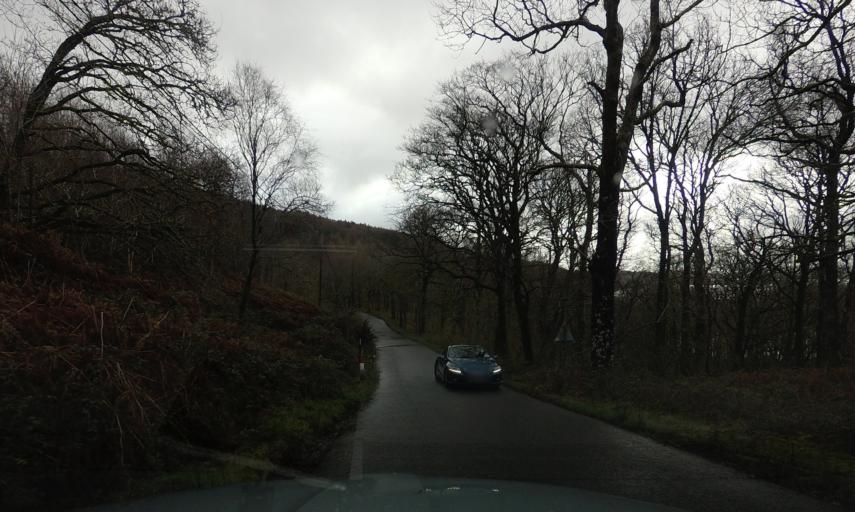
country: GB
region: Scotland
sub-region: West Dunbartonshire
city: Balloch
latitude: 56.1222
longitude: -4.5955
